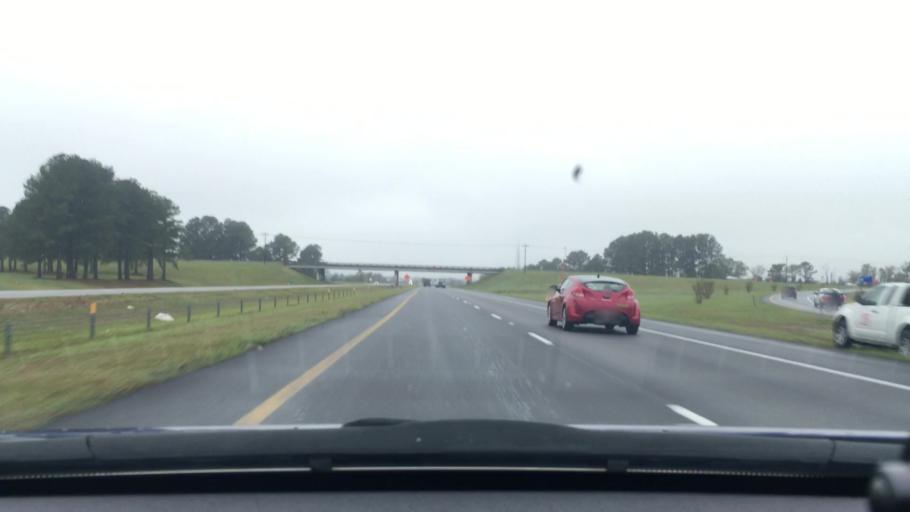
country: US
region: South Carolina
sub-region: Lee County
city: Bishopville
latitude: 34.1867
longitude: -80.2082
